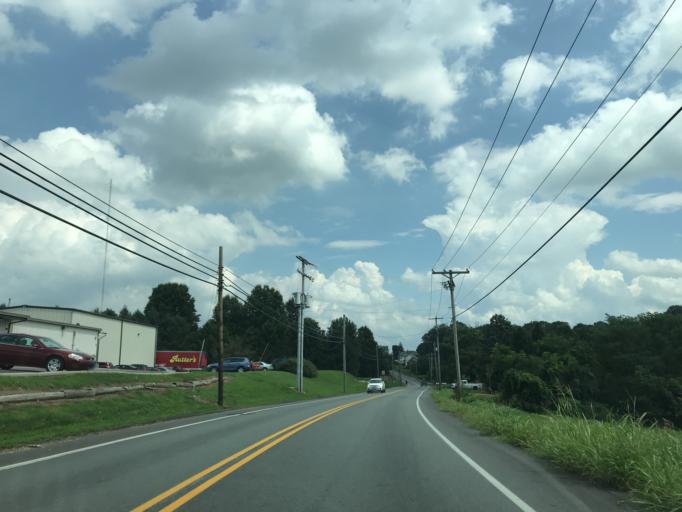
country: US
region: Pennsylvania
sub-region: York County
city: Windsor
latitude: 39.9023
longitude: -76.5873
